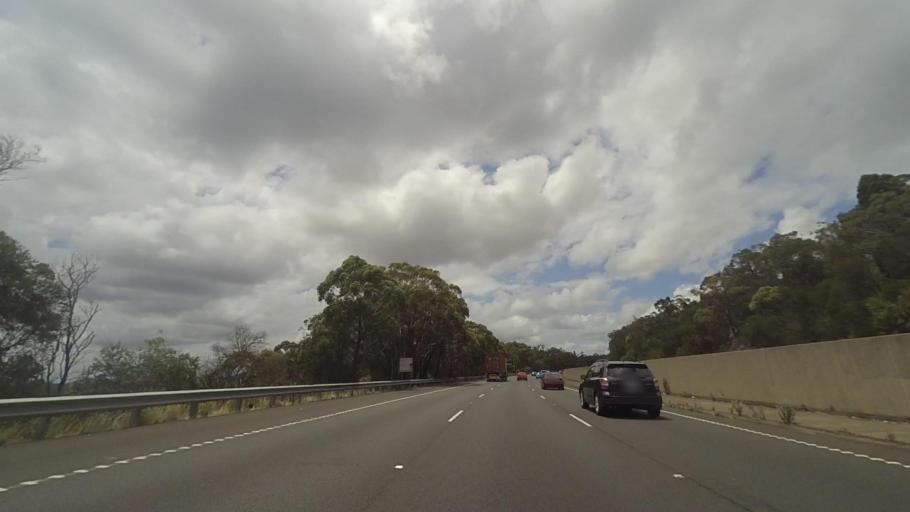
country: AU
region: New South Wales
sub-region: Gosford Shire
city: Point Clare
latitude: -33.4404
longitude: 151.2184
